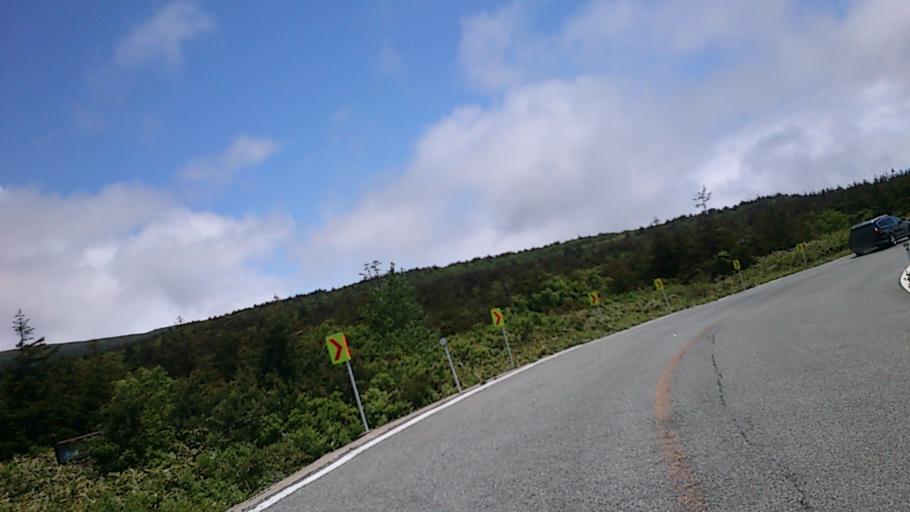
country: JP
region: Yamagata
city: Yamagata-shi
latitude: 38.1250
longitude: 140.4221
